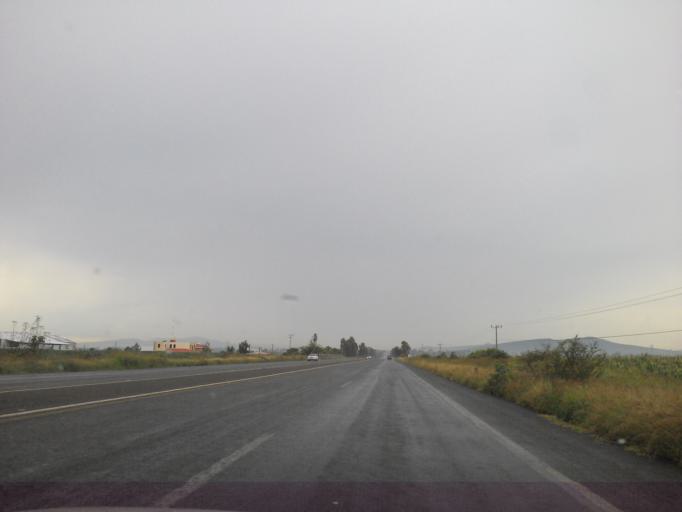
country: MX
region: Jalisco
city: Capilla de Guadalupe
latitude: 20.8755
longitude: -102.6794
